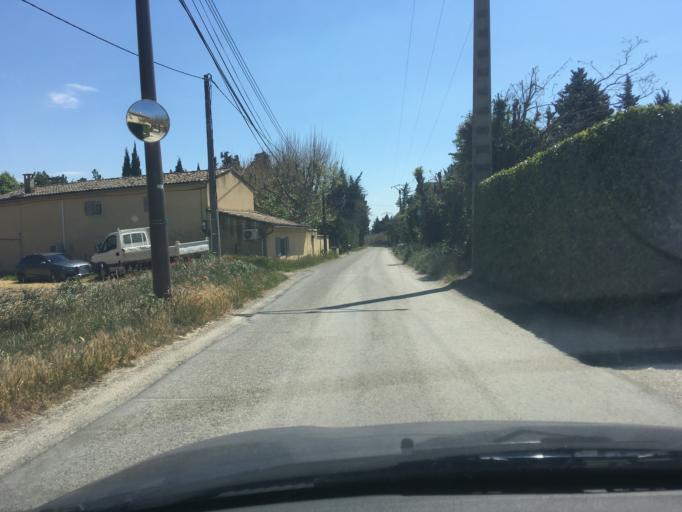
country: FR
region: Provence-Alpes-Cote d'Azur
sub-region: Departement du Vaucluse
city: Sarrians
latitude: 44.1023
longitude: 4.9419
